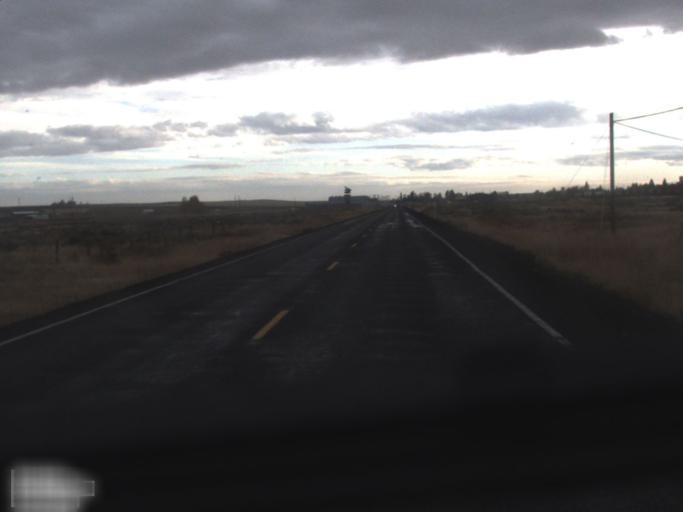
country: US
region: Washington
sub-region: Lincoln County
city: Davenport
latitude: 47.6681
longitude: -118.1410
